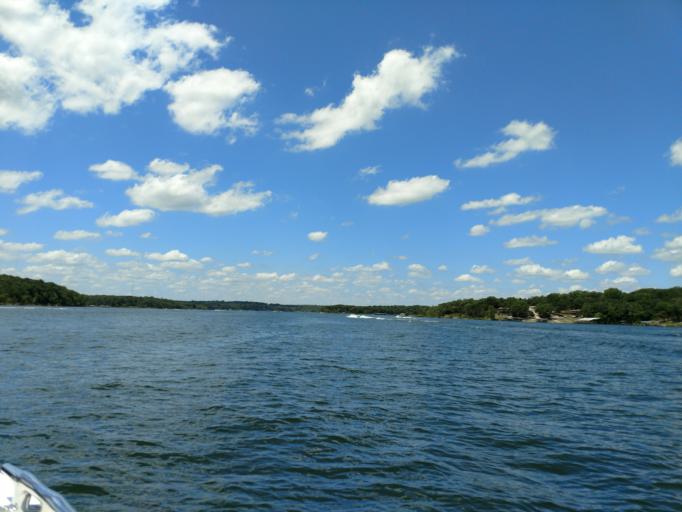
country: US
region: Missouri
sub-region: Barry County
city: Shell Knob
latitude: 36.5900
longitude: -93.5514
